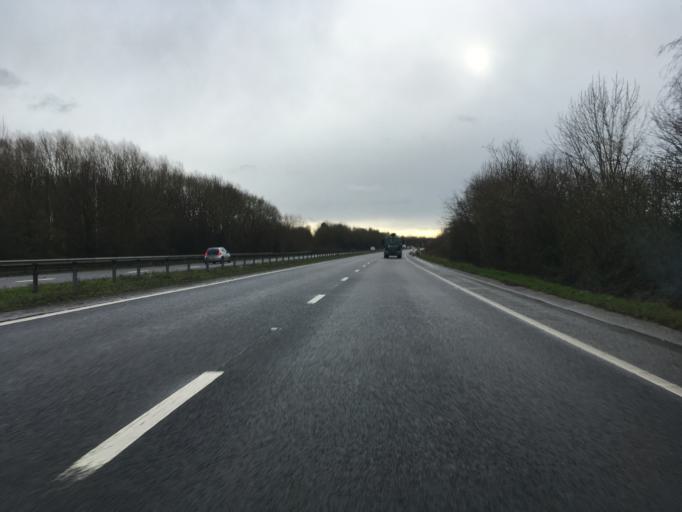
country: GB
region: England
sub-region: Warwickshire
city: Alcester
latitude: 52.1929
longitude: -1.8764
